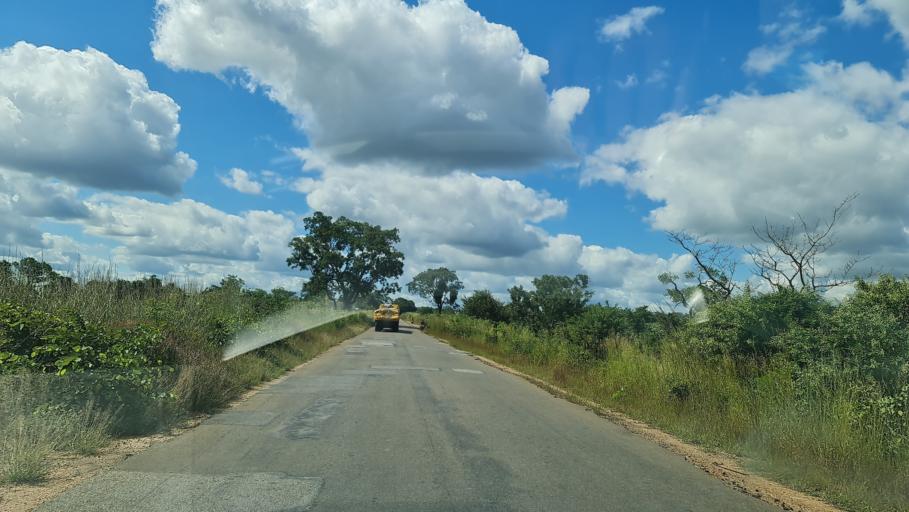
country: MZ
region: Zambezia
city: Quelimane
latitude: -17.5128
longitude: 36.2255
